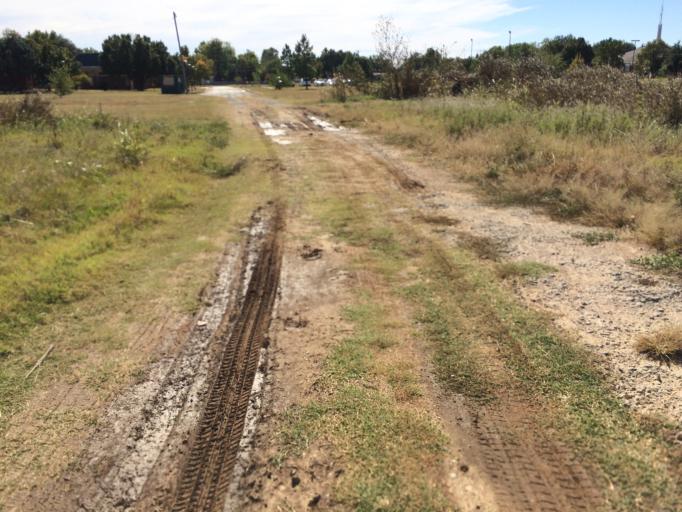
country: US
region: Oklahoma
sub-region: Cleveland County
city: Norman
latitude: 35.2207
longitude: -97.4282
